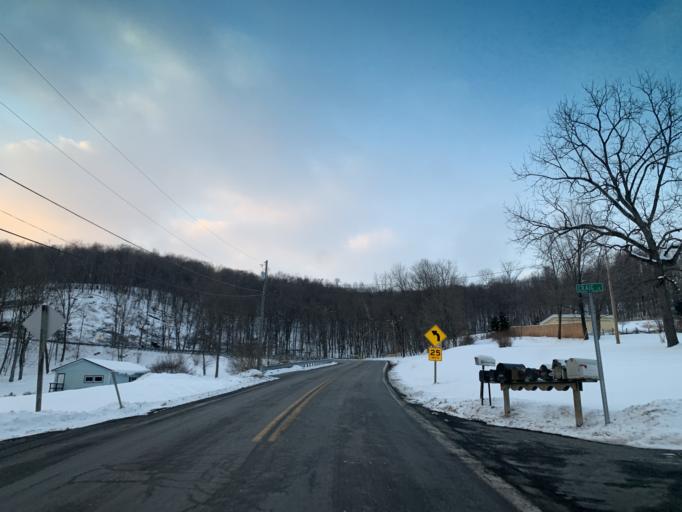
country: US
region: Maryland
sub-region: Allegany County
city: Frostburg
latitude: 39.6646
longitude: -78.9225
